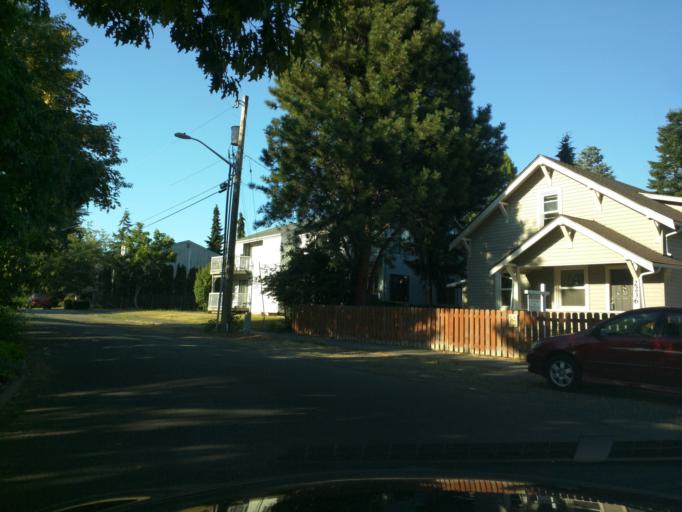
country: US
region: Washington
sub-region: Whatcom County
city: Bellingham
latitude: 48.7602
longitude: -122.4481
